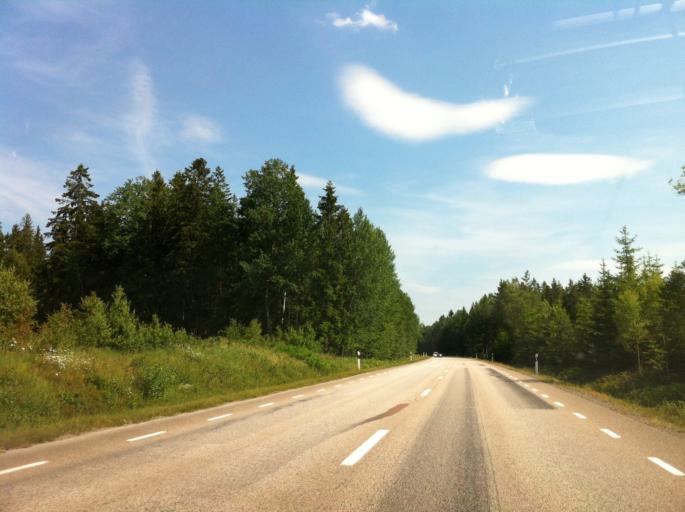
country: SE
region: Kalmar
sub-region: Nybro Kommun
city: Nybro
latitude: 56.8253
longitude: 15.7549
